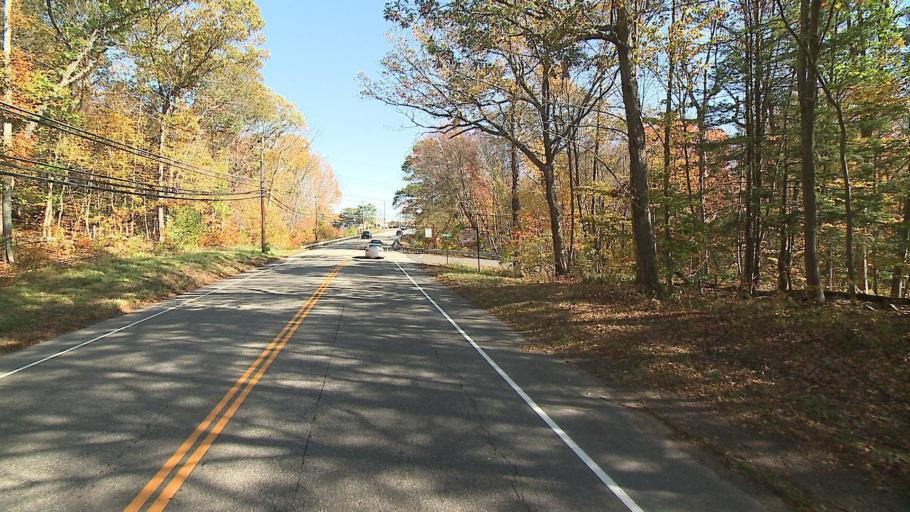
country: US
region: Connecticut
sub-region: Tolland County
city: Rockville
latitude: 41.7942
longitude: -72.4374
